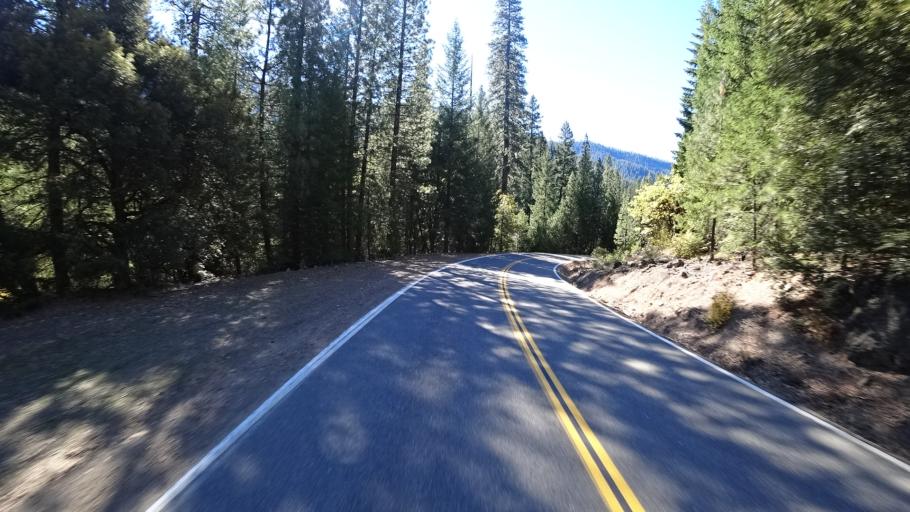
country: US
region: California
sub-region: Trinity County
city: Weaverville
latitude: 41.2237
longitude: -123.0171
